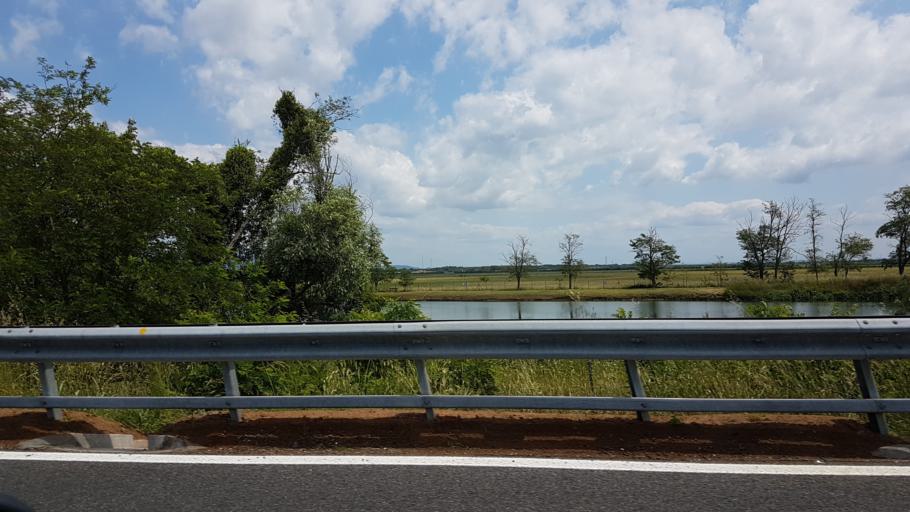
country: IT
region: Tuscany
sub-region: Provincia di Livorno
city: Guasticce
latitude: 43.6149
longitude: 10.3574
